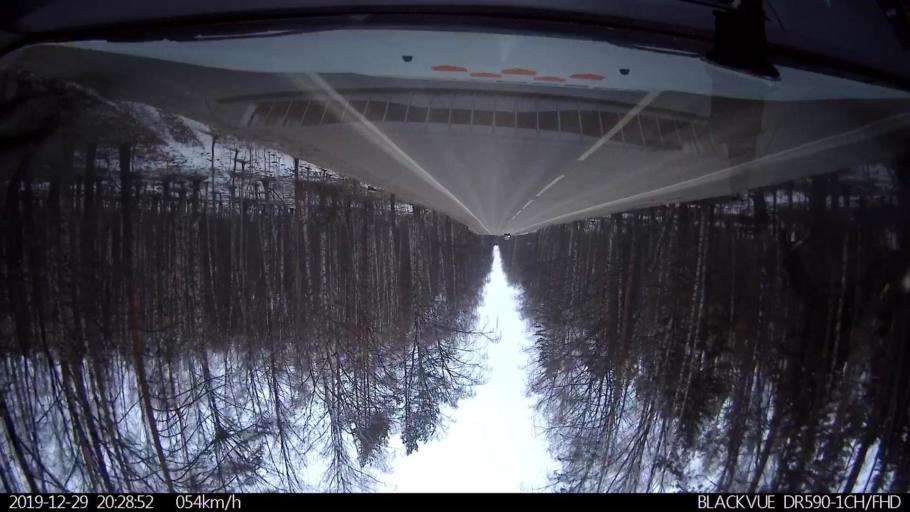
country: RU
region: Nizjnij Novgorod
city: Afonino
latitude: 56.1843
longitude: 44.1092
